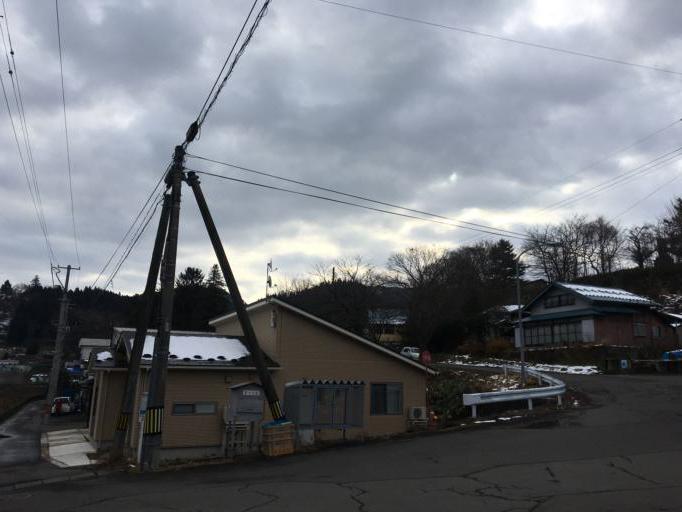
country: JP
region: Aomori
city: Hirosaki
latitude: 40.5197
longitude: 140.5660
